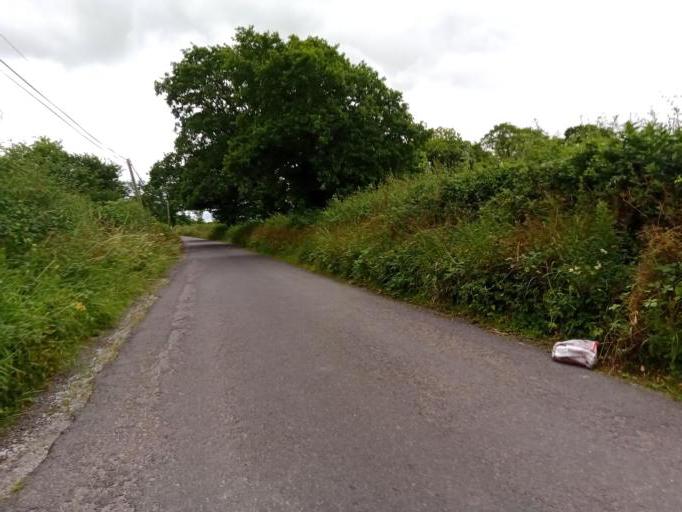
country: IE
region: Leinster
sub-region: Kilkenny
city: Callan
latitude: 52.5709
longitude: -7.3776
